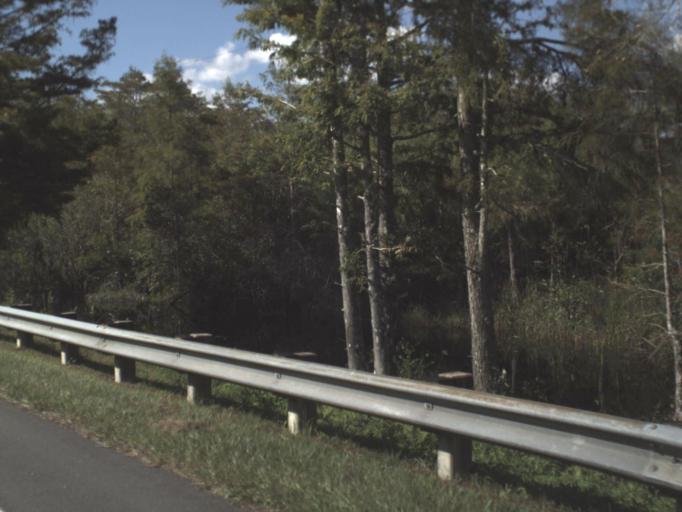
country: US
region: Florida
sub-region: Collier County
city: Marco
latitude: 25.8788
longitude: -81.2416
